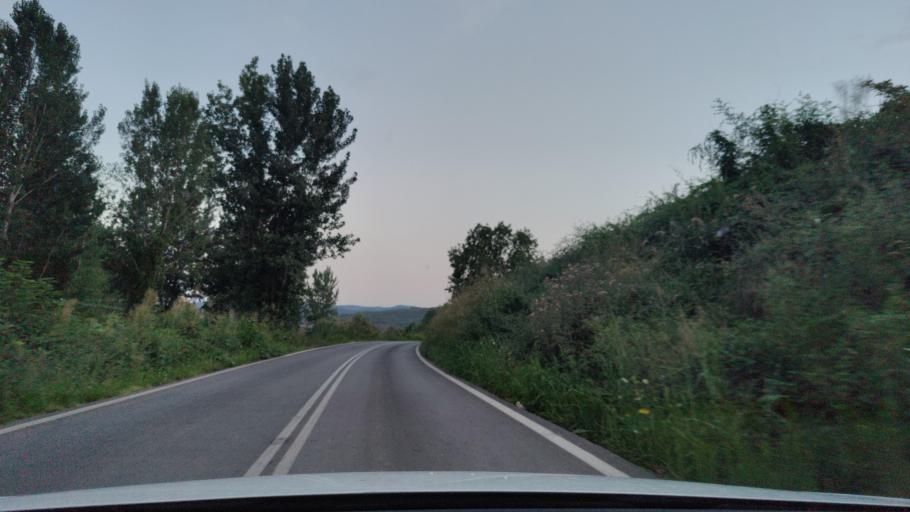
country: GR
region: Central Macedonia
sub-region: Nomos Serron
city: Chrysochorafa
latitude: 41.1415
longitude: 23.2286
